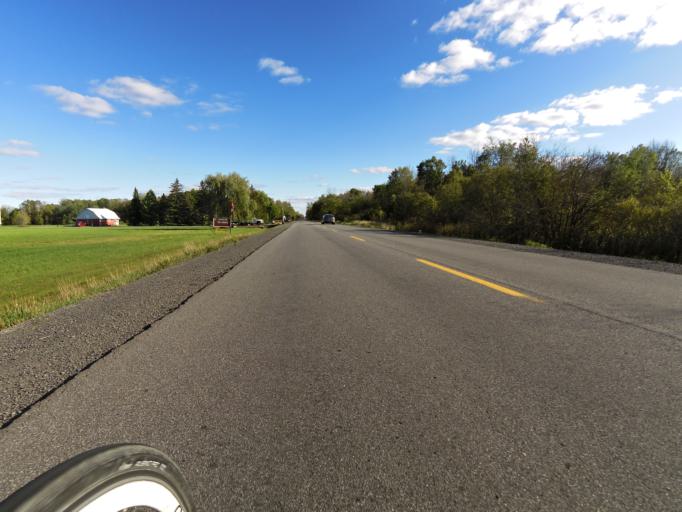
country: CA
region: Ontario
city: Bells Corners
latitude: 45.1581
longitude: -75.7822
